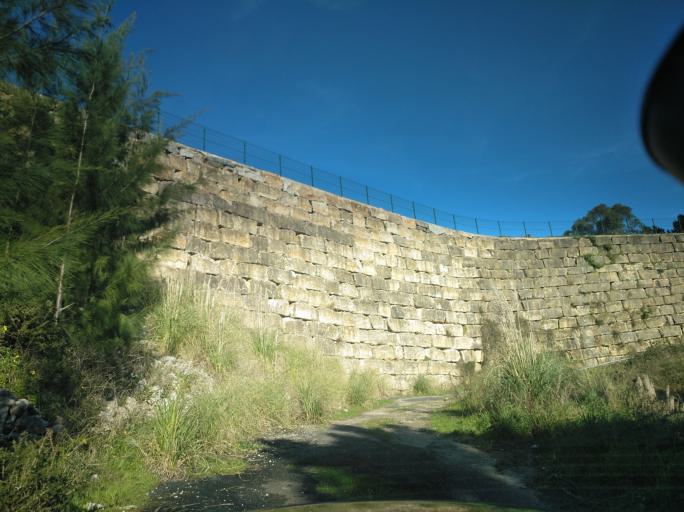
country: PT
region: Lisbon
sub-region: Mafra
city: Mafra
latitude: 38.9346
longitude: -9.3137
